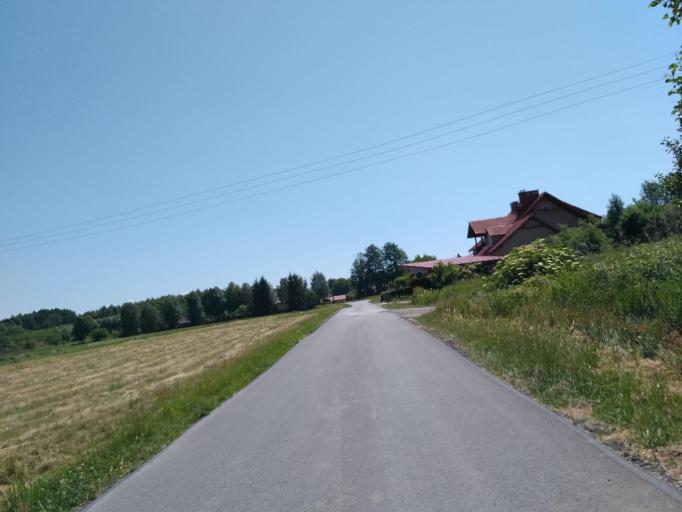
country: PL
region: Subcarpathian Voivodeship
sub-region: Krosno
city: Krosno
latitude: 49.7132
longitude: 21.7820
